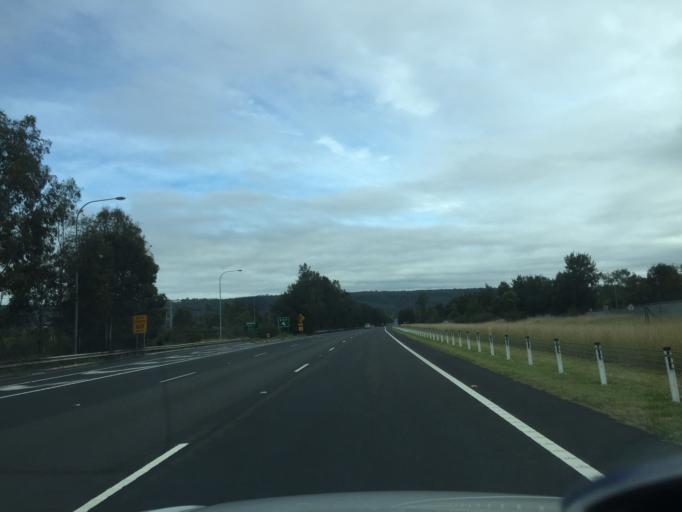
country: AU
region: New South Wales
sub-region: Penrith Municipality
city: Glenmore Park
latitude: -33.7752
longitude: 150.6733
